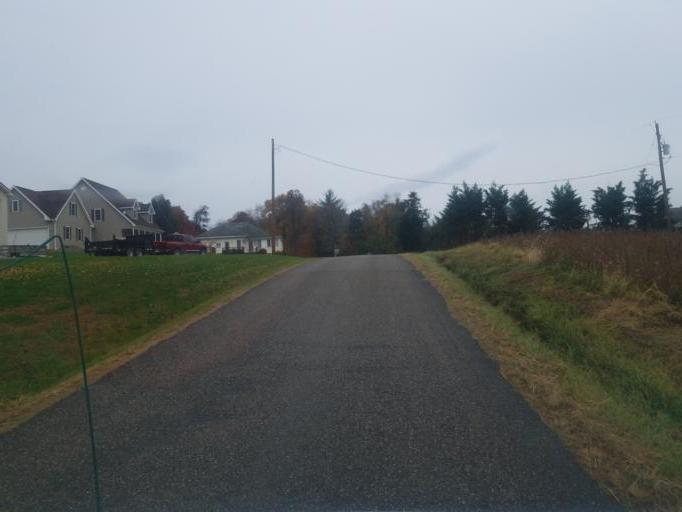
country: US
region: Ohio
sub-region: Washington County
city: Beverly
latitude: 39.5458
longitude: -81.7044
